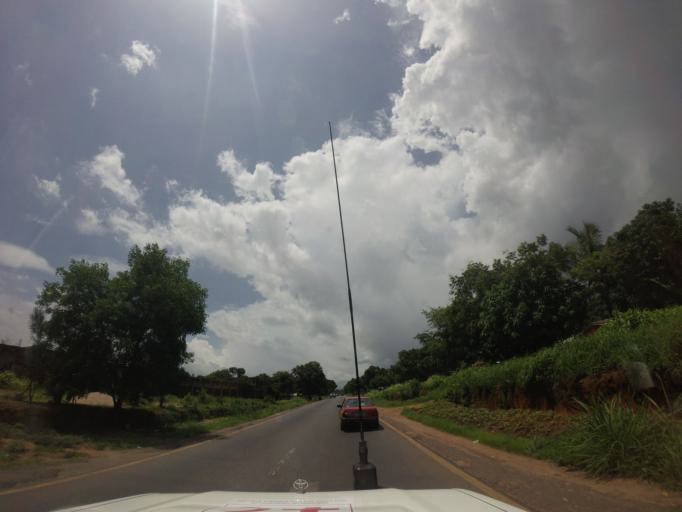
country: SL
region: Western Area
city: Waterloo
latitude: 8.3352
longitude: -13.0233
